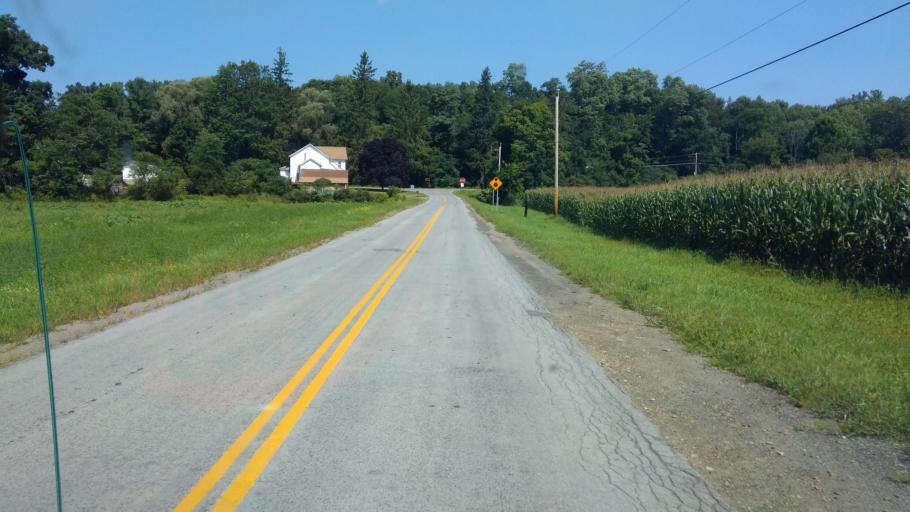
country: US
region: New York
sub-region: Allegany County
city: Belmont
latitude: 42.2964
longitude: -78.0574
